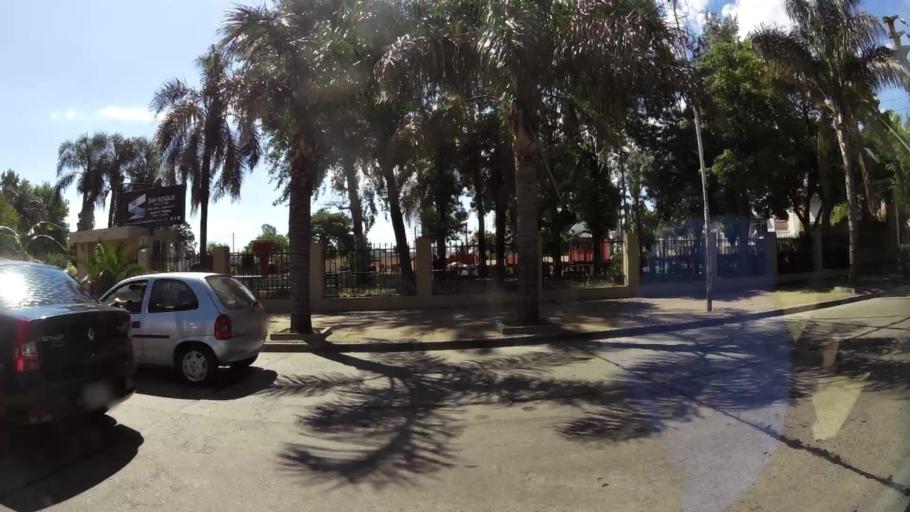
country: AR
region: Buenos Aires
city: San Justo
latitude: -34.6680
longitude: -58.5539
